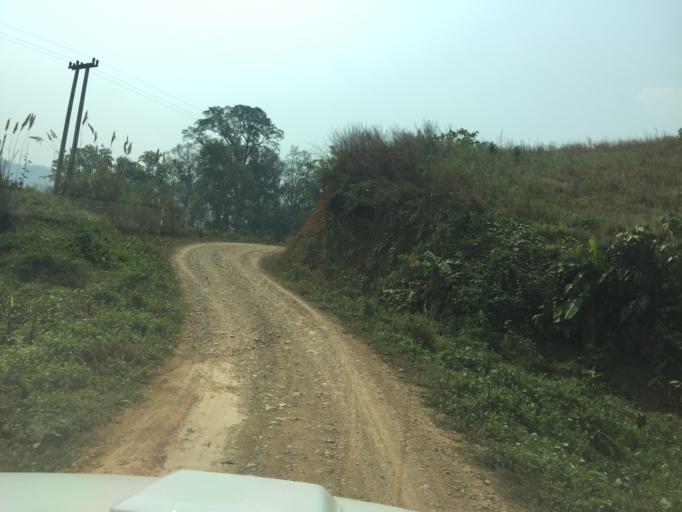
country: TH
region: Phayao
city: Phu Sang
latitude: 19.5853
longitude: 100.5256
